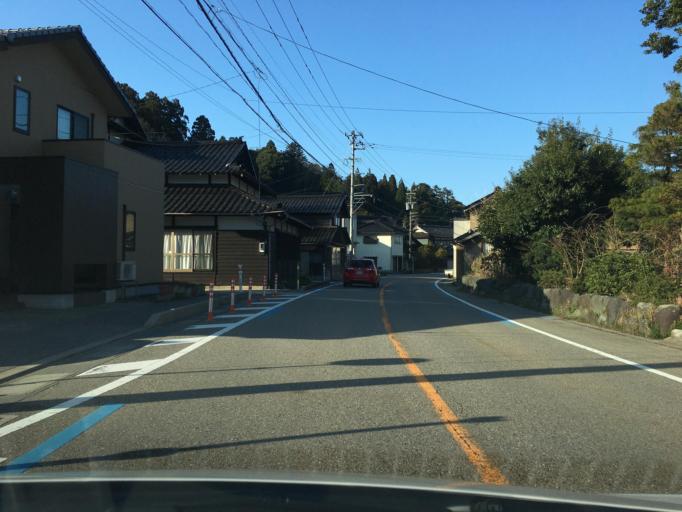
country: JP
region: Toyama
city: Himi
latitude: 36.9322
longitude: 137.0261
